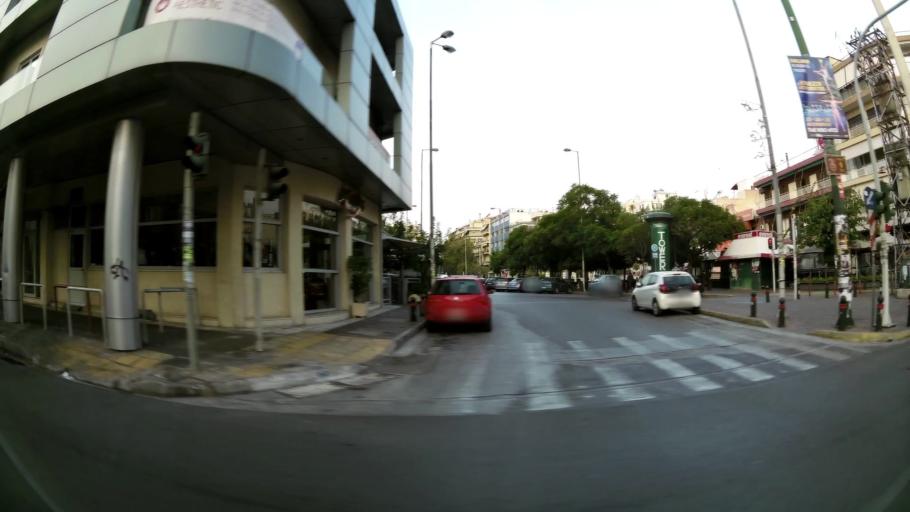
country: GR
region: Attica
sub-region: Nomarchia Athinas
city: Dhafni
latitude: 37.9496
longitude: 23.7382
